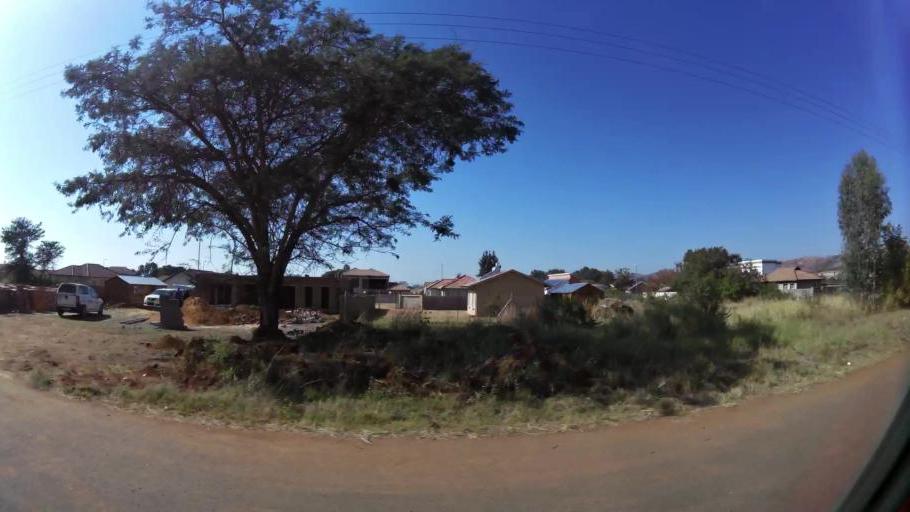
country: ZA
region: Gauteng
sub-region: City of Tshwane Metropolitan Municipality
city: Pretoria
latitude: -25.6663
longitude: 28.1013
